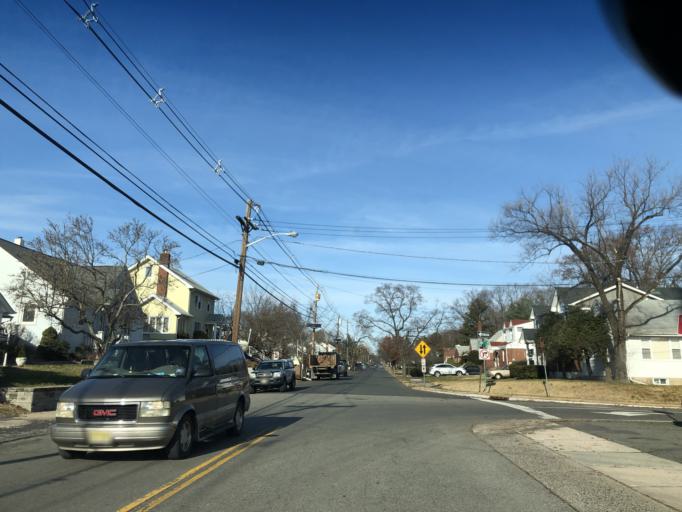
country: US
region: New Jersey
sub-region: Bergen County
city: Elmwood Park
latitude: 40.9218
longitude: -74.1176
